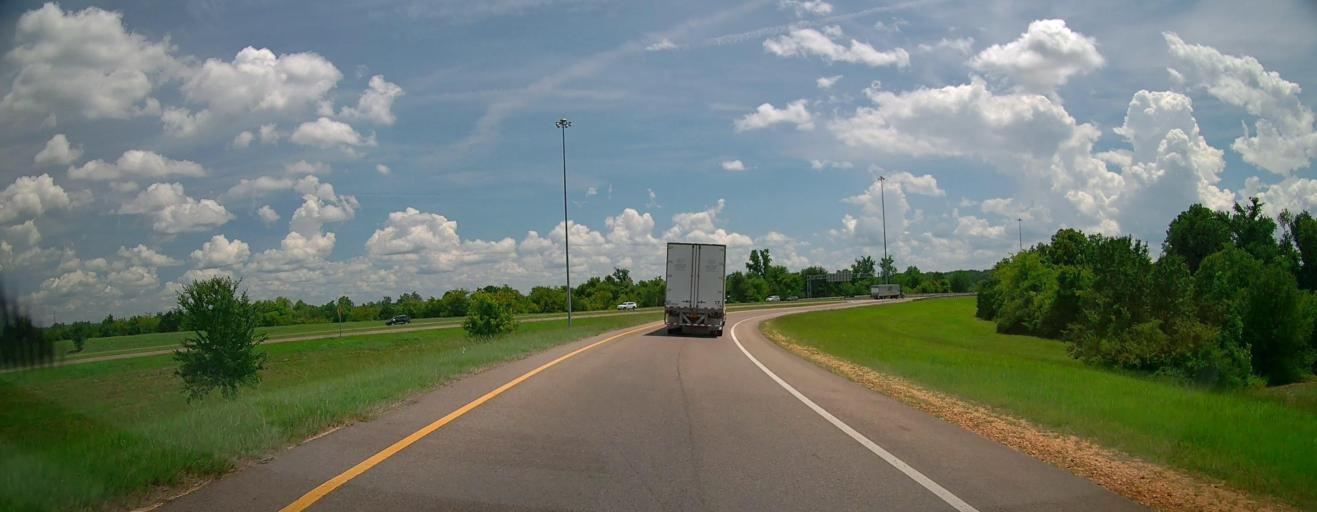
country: US
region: Mississippi
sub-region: Lee County
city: Tupelo
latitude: 34.2938
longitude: -88.7049
